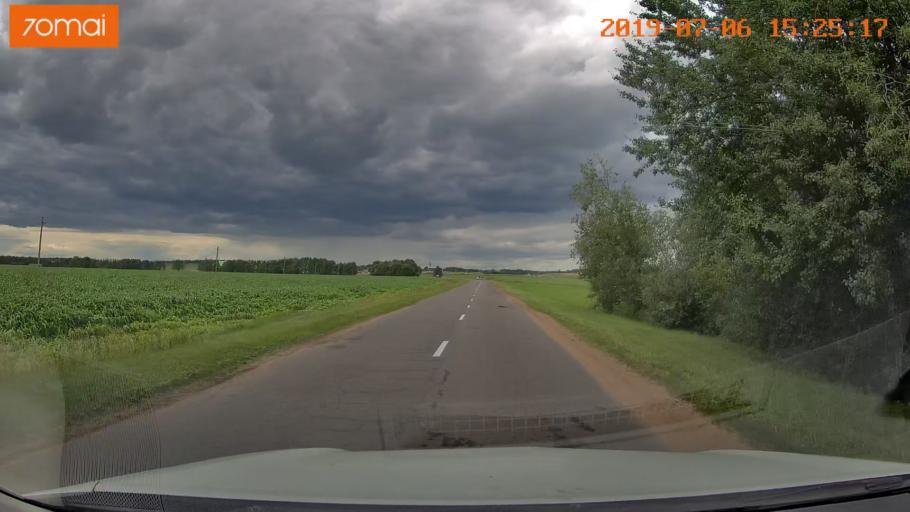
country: BY
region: Minsk
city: Valozhyn
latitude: 54.0298
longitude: 26.6039
